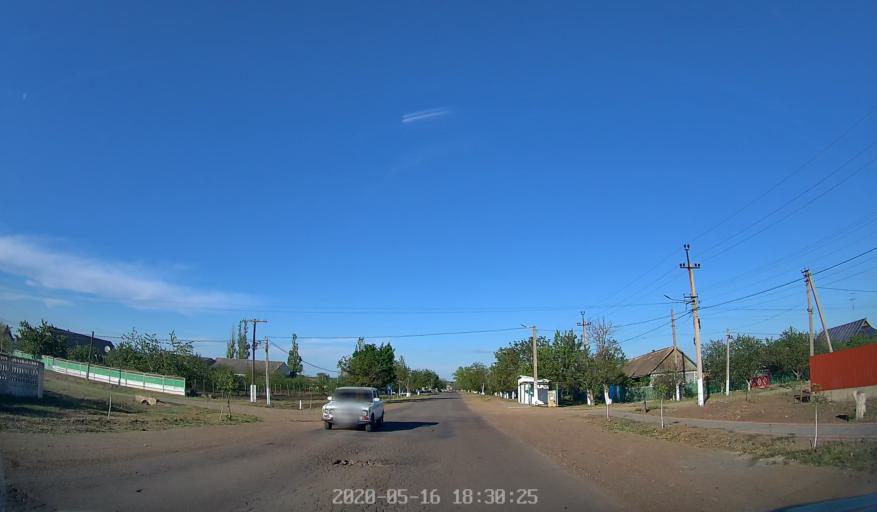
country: UA
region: Odessa
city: Lymanske
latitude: 46.5389
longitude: 30.0305
